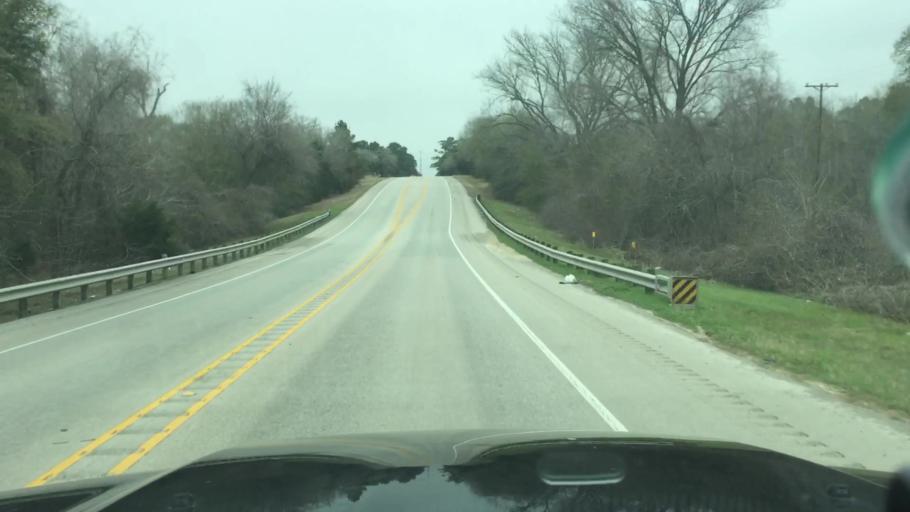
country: US
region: Texas
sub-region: Fayette County
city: La Grange
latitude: 30.0041
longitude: -96.8932
